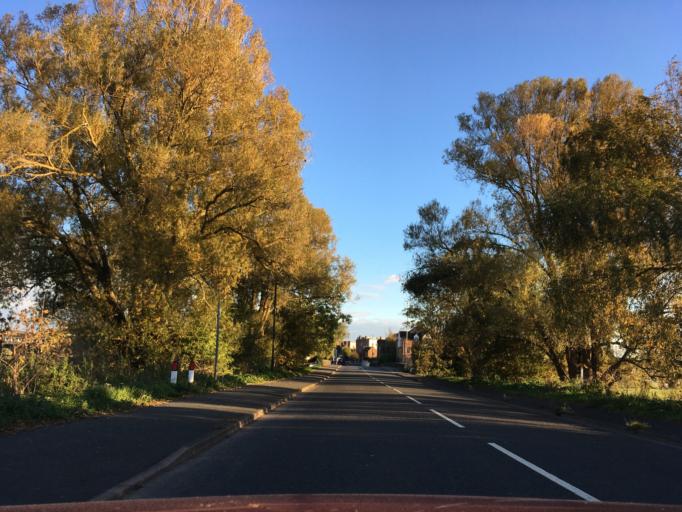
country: GB
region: England
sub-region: Gloucestershire
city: Tewkesbury
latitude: 51.9991
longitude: -2.1581
